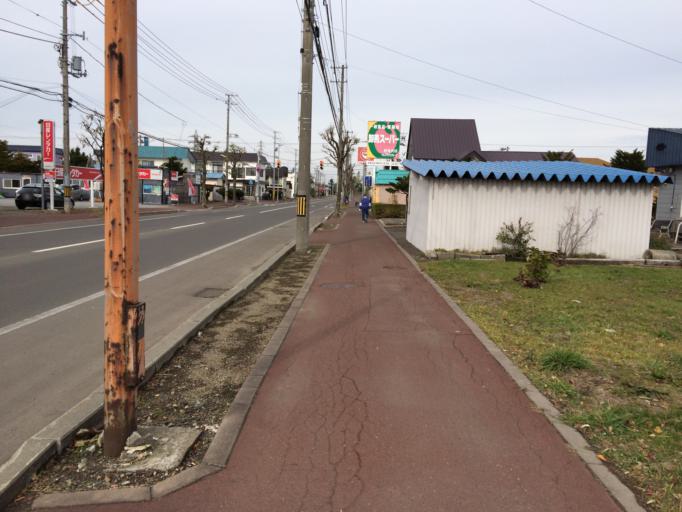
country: JP
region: Hokkaido
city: Iwamizawa
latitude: 43.2056
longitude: 141.7511
